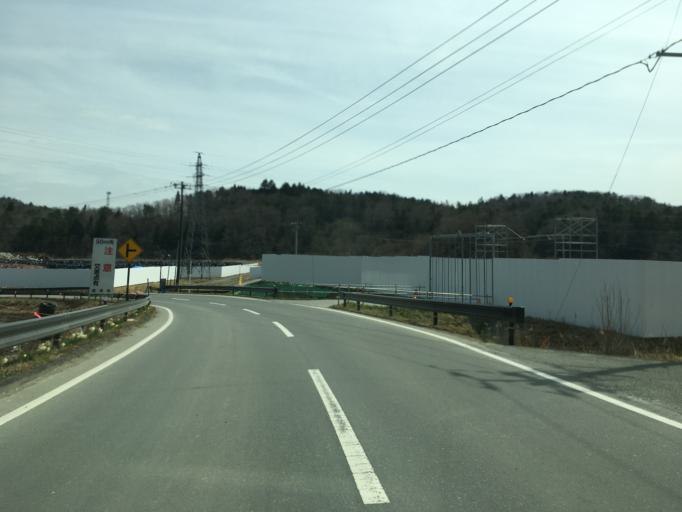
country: JP
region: Fukushima
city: Namie
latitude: 37.4544
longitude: 140.9762
